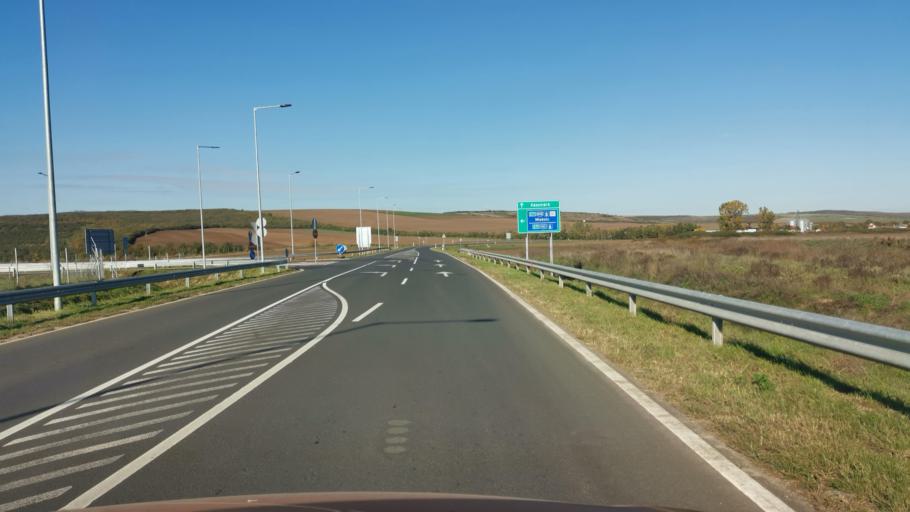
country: HU
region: Borsod-Abauj-Zemplen
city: Halmaj
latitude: 48.2546
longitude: 20.9790
